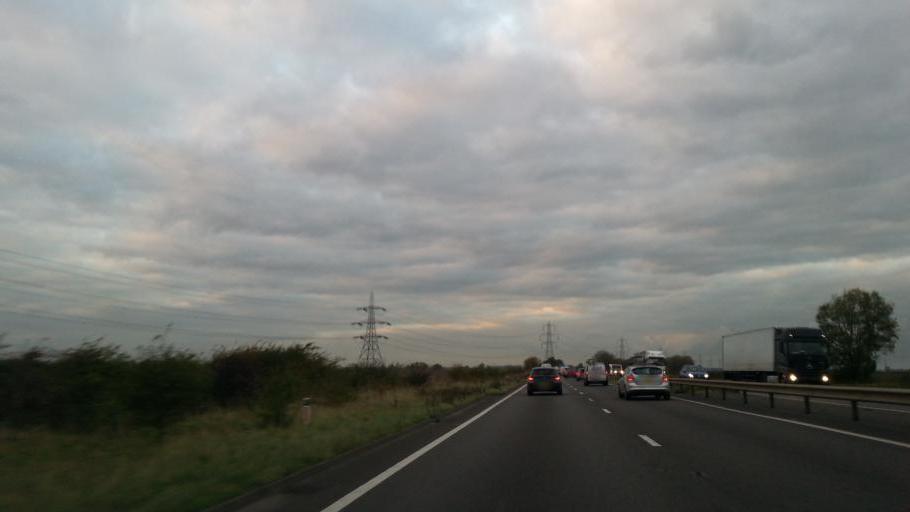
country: GB
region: England
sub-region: Lincolnshire
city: Long Bennington
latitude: 53.0064
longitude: -0.7629
